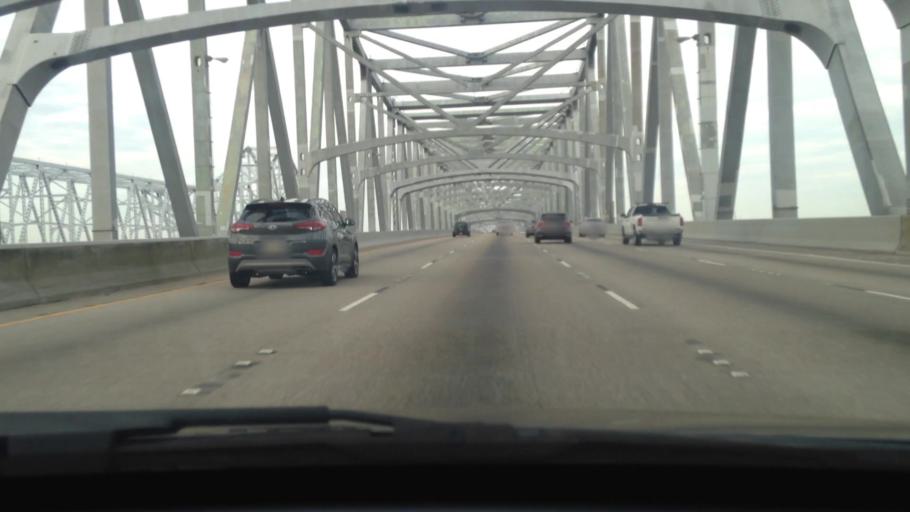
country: US
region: Louisiana
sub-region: Jefferson Parish
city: Gretna
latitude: 29.9389
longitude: -90.0538
